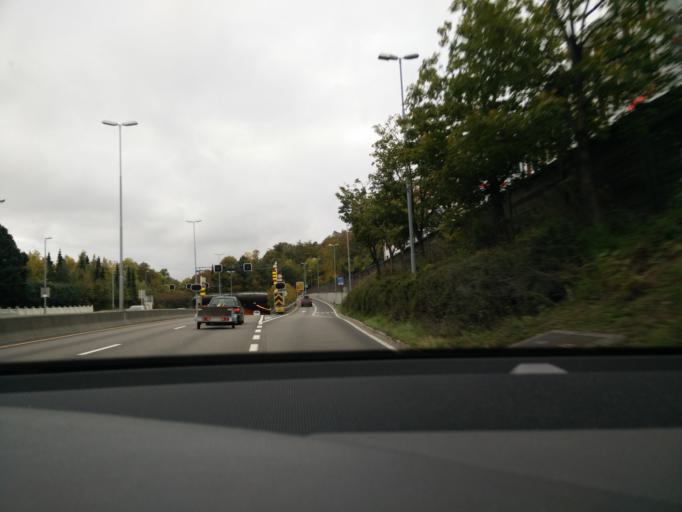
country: NO
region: Akershus
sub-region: Baerum
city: Lysaker
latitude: 59.9269
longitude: 10.6524
